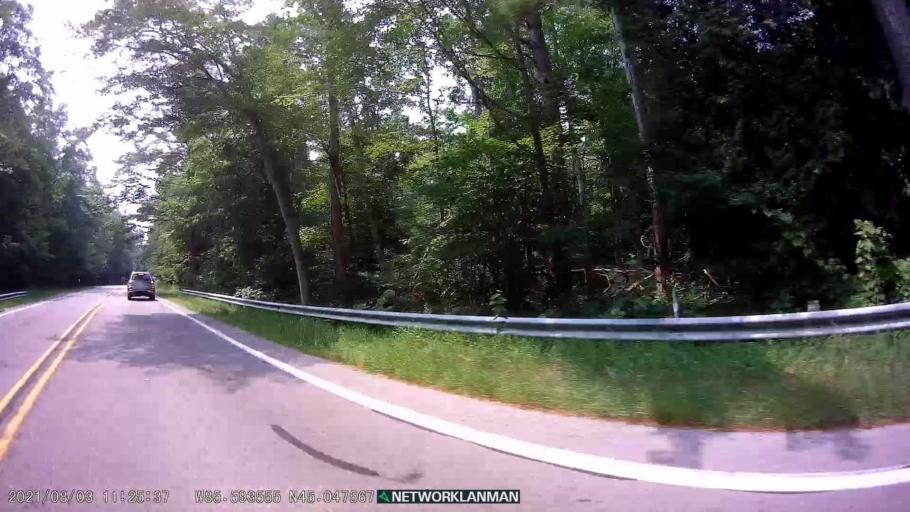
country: US
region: Michigan
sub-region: Leelanau County
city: Leland
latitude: 45.0473
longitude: -85.5940
